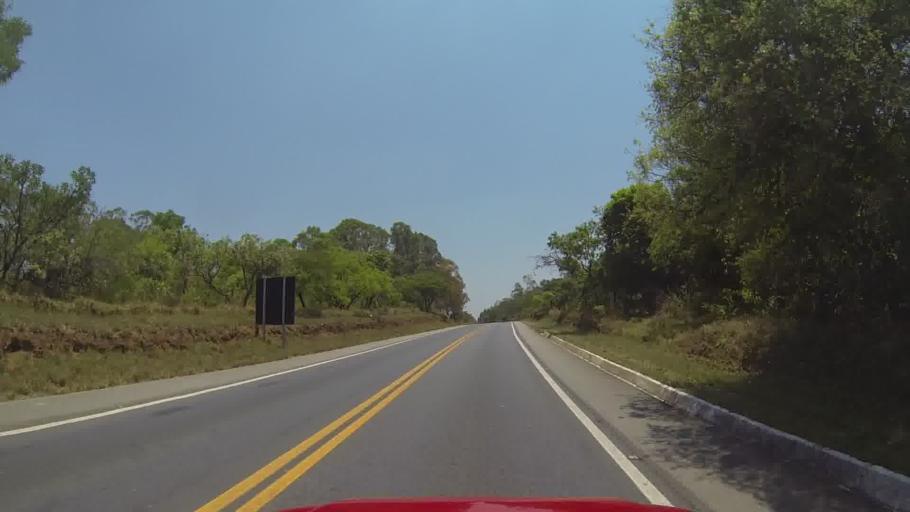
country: BR
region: Minas Gerais
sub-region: Itapecerica
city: Itapecerica
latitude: -20.3087
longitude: -45.2079
